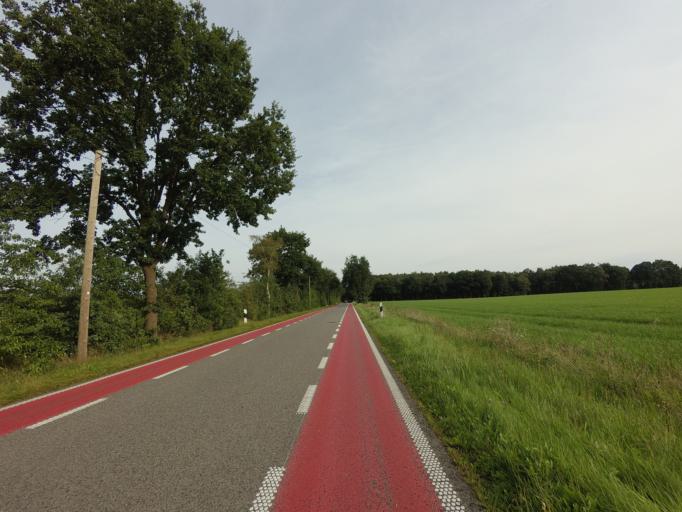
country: DE
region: Lower Saxony
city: Getelo
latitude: 52.4649
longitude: 6.8464
